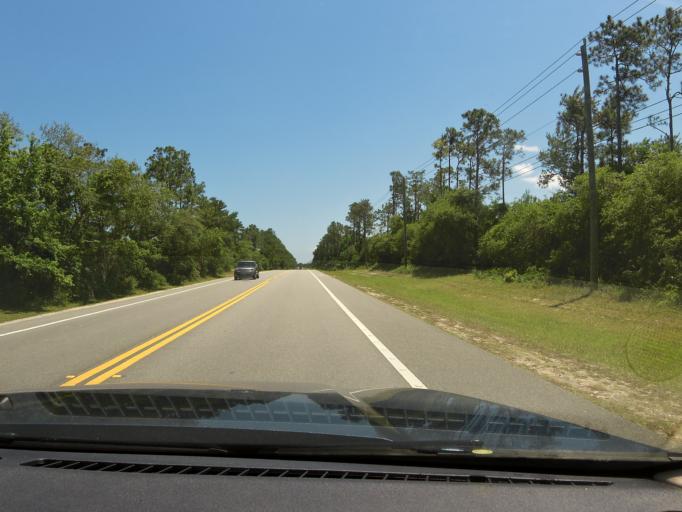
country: US
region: Florida
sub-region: Flagler County
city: Flagler Beach
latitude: 29.4691
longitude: -81.1745
